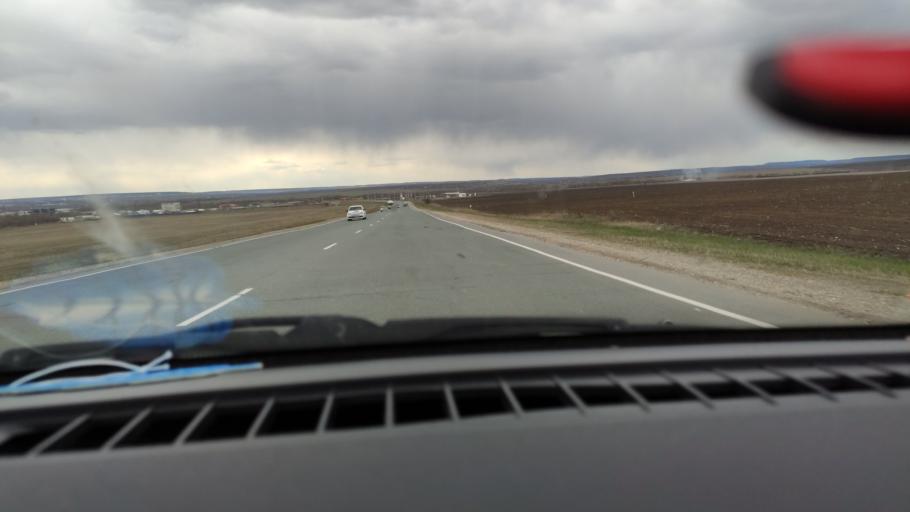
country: RU
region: Saratov
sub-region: Saratovskiy Rayon
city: Saratov
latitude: 51.7381
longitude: 46.0405
